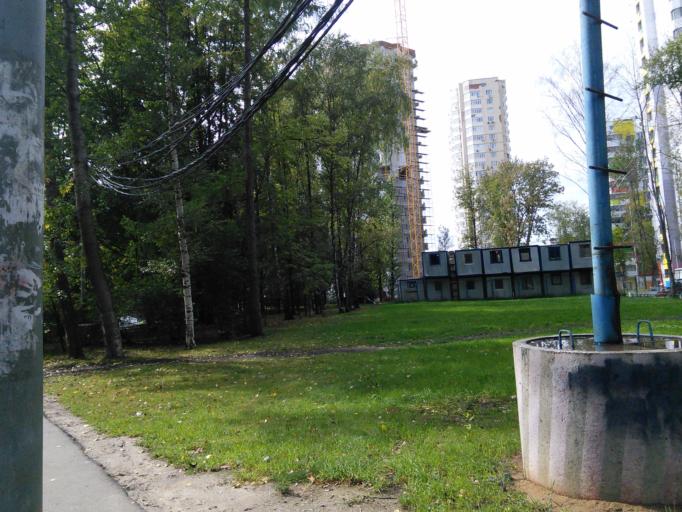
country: RU
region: Moscow
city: Nikol'skoye
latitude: 55.6740
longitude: 37.4992
